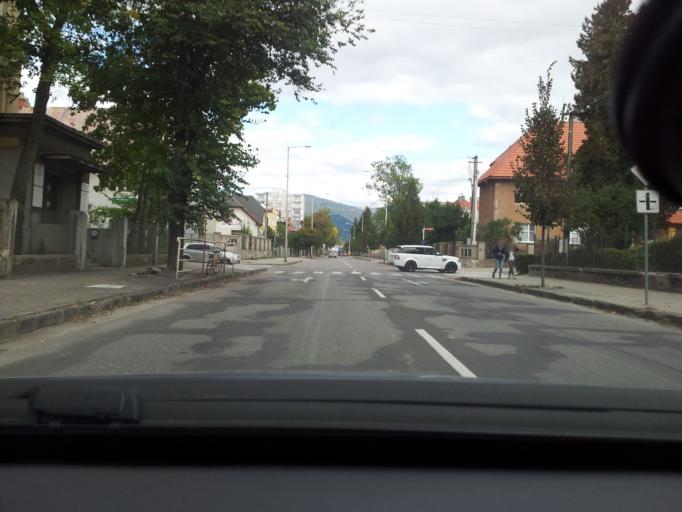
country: SK
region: Zilinsky
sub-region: Okres Martin
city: Martin
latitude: 49.0670
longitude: 18.9263
